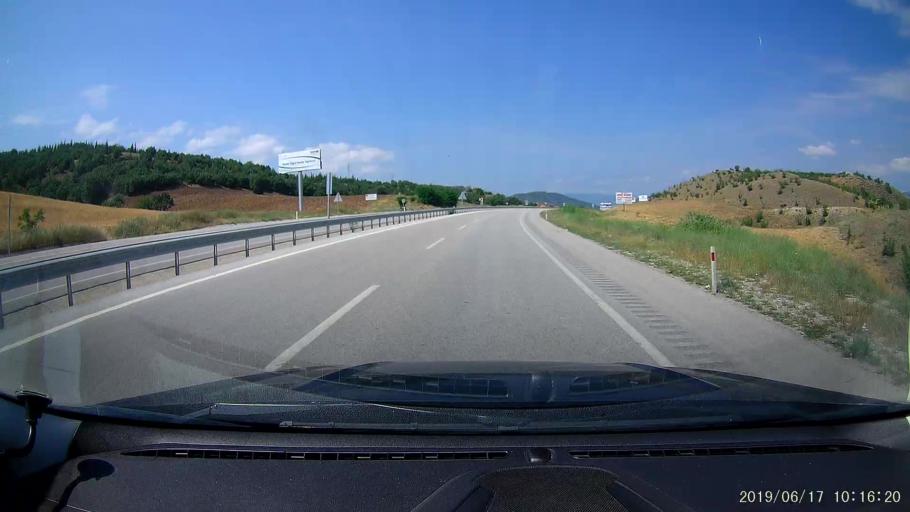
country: TR
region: Amasya
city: Saraycik
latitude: 40.9911
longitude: 34.9780
